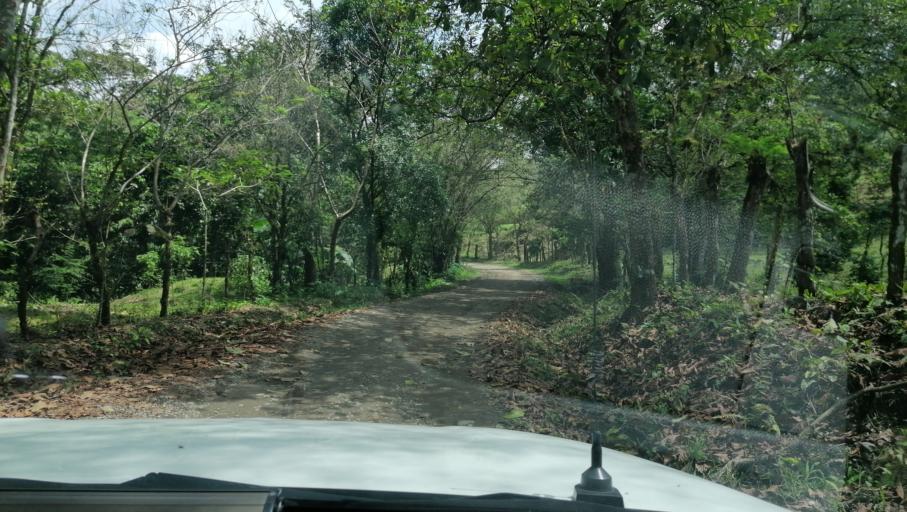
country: MX
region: Chiapas
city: Ixtacomitan
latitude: 17.4444
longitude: -93.1776
